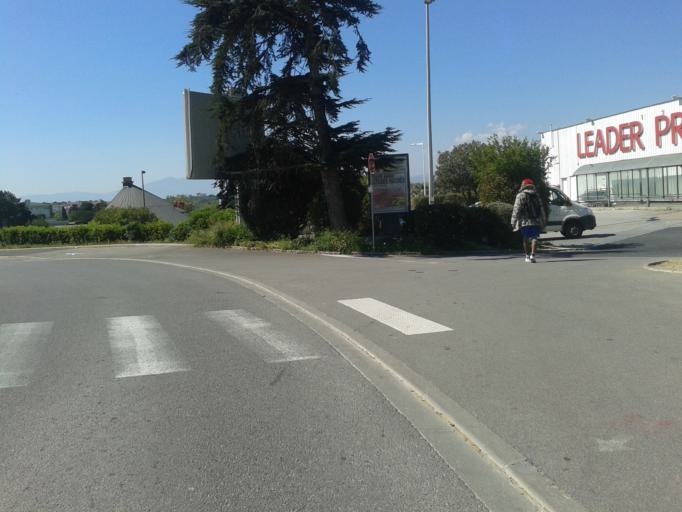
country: FR
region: Languedoc-Roussillon
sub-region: Departement des Pyrenees-Orientales
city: Perpignan
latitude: 42.6819
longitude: 2.8960
